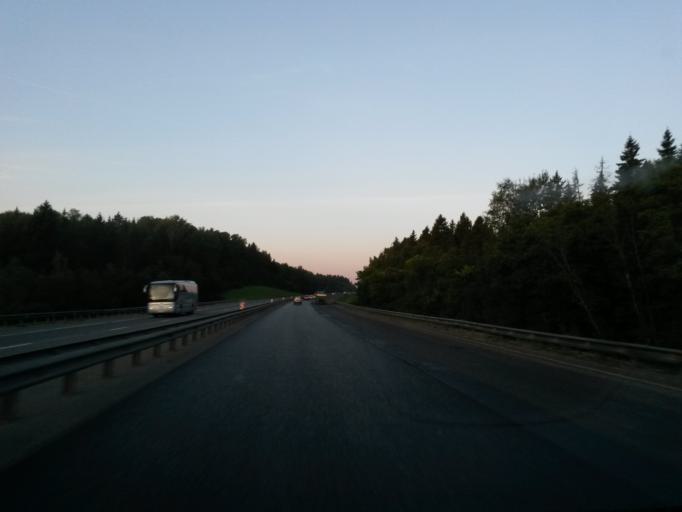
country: RU
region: Moskovskaya
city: Svatkovo
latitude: 56.2977
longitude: 38.2318
